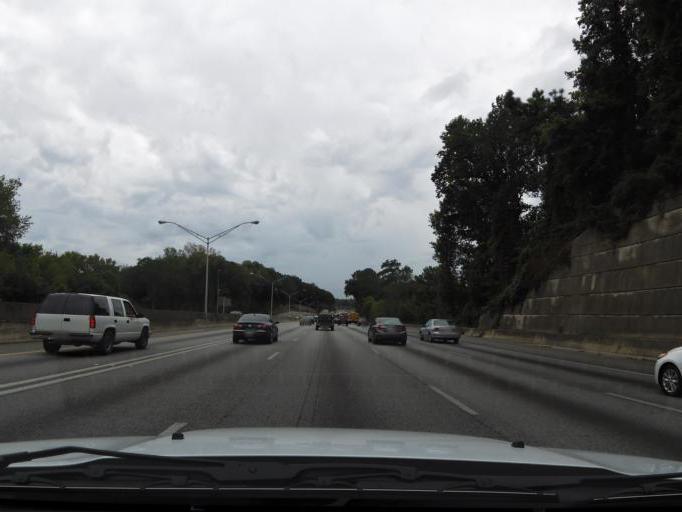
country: US
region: Georgia
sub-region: Cobb County
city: Vinings
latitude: 33.8259
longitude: -84.4241
